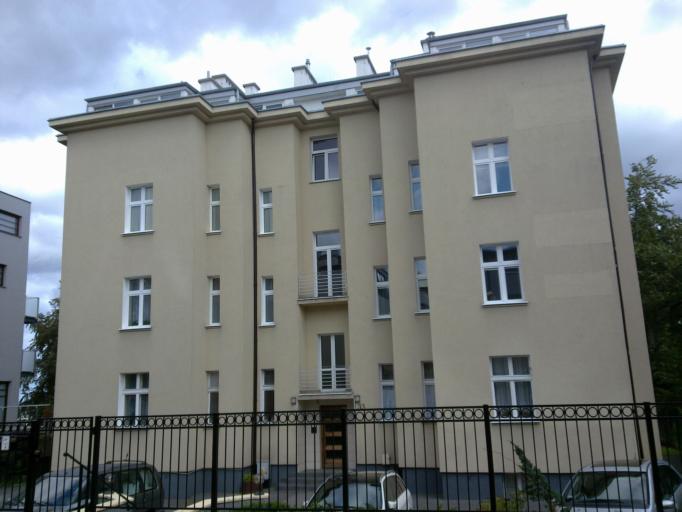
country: PL
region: Pomeranian Voivodeship
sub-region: Gdynia
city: Gdynia
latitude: 54.5118
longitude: 18.5492
